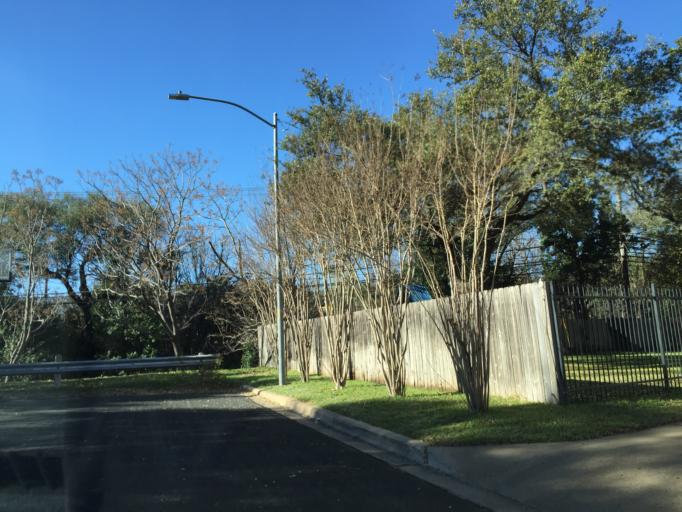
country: US
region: Texas
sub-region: Williamson County
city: Jollyville
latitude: 30.4010
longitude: -97.7316
